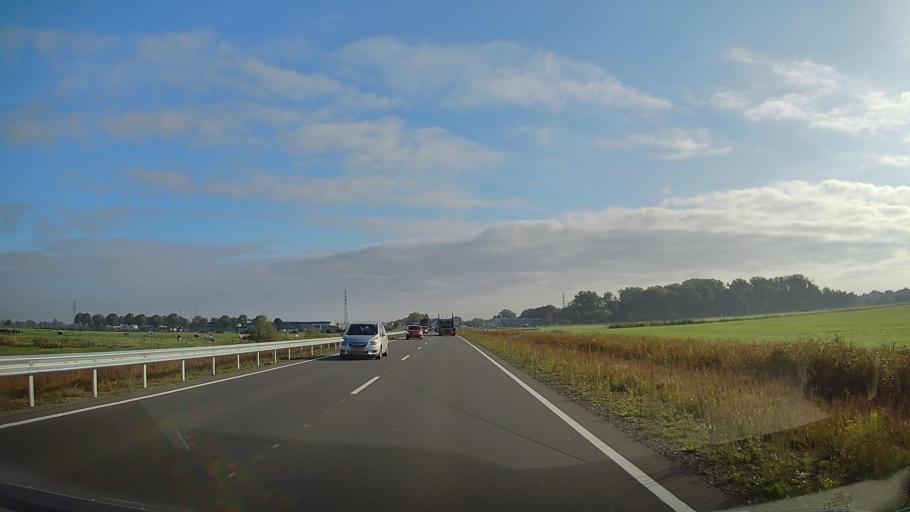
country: DE
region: Lower Saxony
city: Brake (Unterweser)
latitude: 53.3294
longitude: 8.4514
